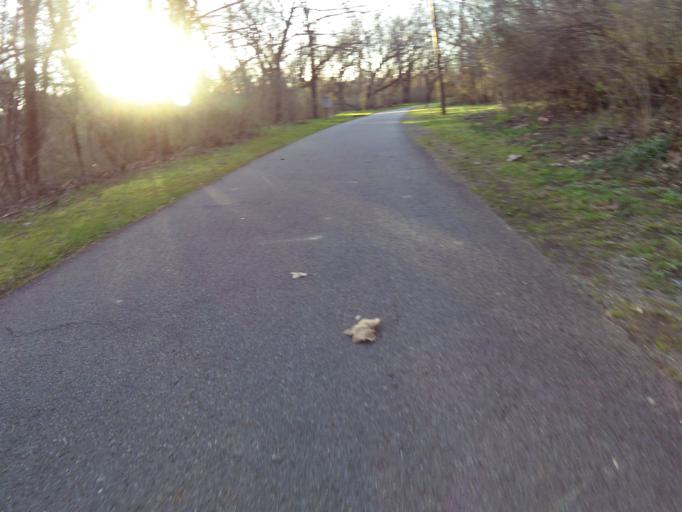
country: US
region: Tennessee
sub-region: Blount County
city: Maryville
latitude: 35.7590
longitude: -83.9773
